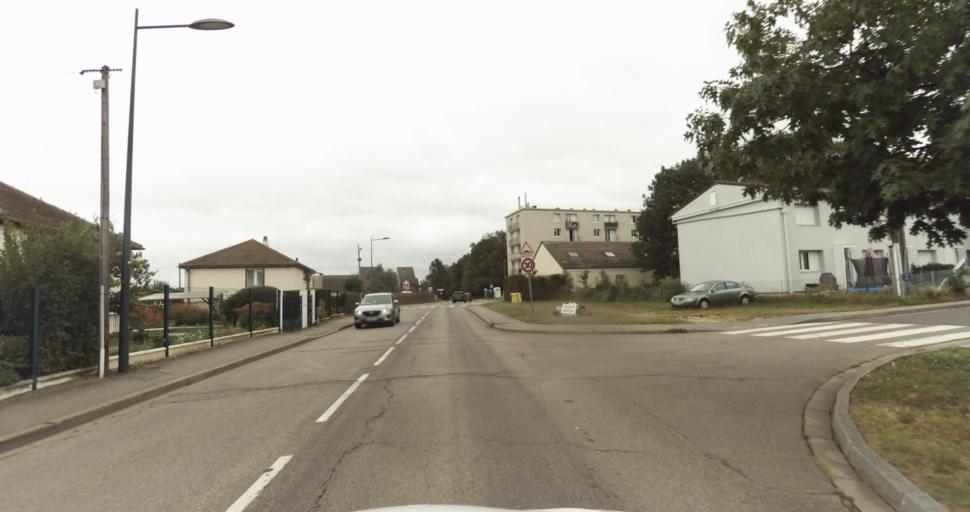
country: FR
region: Haute-Normandie
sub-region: Departement de l'Eure
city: Gravigny
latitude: 49.0286
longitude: 1.1799
